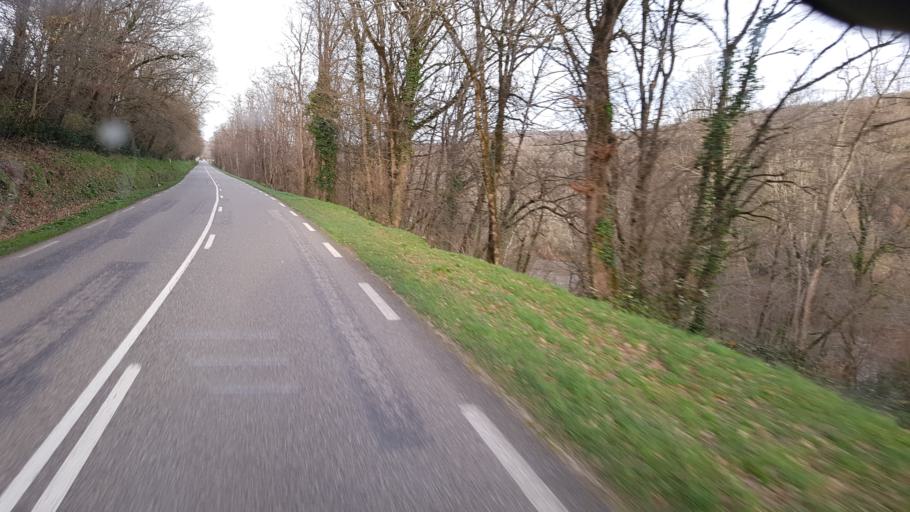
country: FR
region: Midi-Pyrenees
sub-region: Departement du Tarn-et-Garonne
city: Montricoux
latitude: 44.0663
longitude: 1.6576
